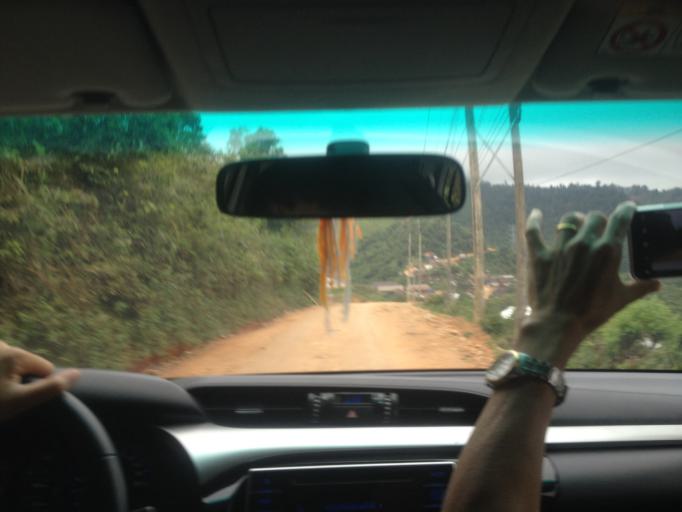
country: TH
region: Nan
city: Chaloem Phra Kiat
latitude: 19.9976
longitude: 101.1289
